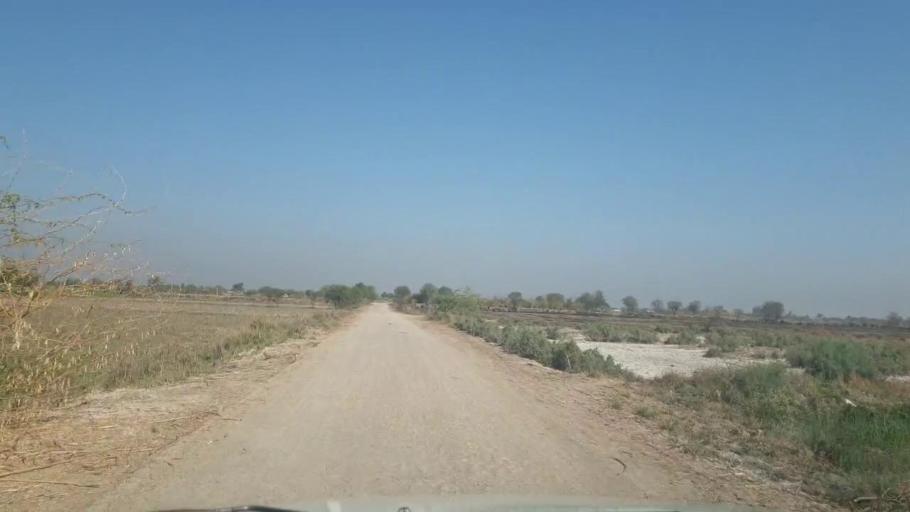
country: PK
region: Sindh
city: Mirpur Khas
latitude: 25.5107
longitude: 69.1498
